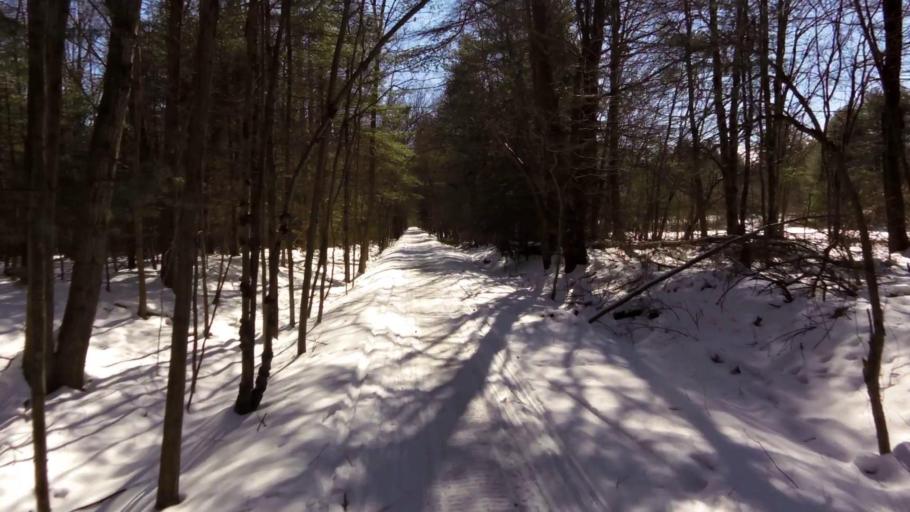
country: US
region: New York
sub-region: Allegany County
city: Houghton
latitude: 42.3578
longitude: -78.1307
